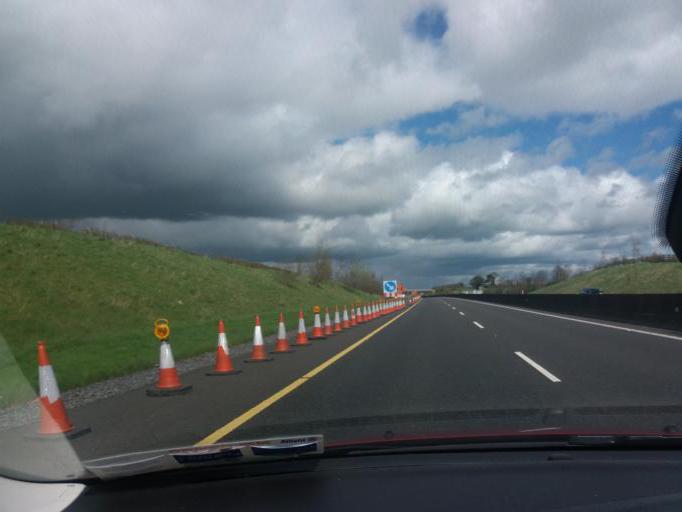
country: IE
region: Leinster
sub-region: Laois
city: Rathdowney
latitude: 52.7450
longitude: -7.5754
